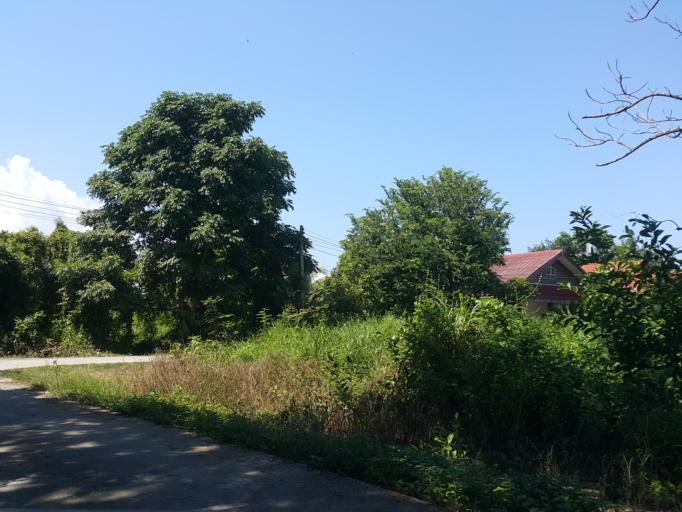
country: TH
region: Chiang Mai
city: Saraphi
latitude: 18.7664
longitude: 99.0601
